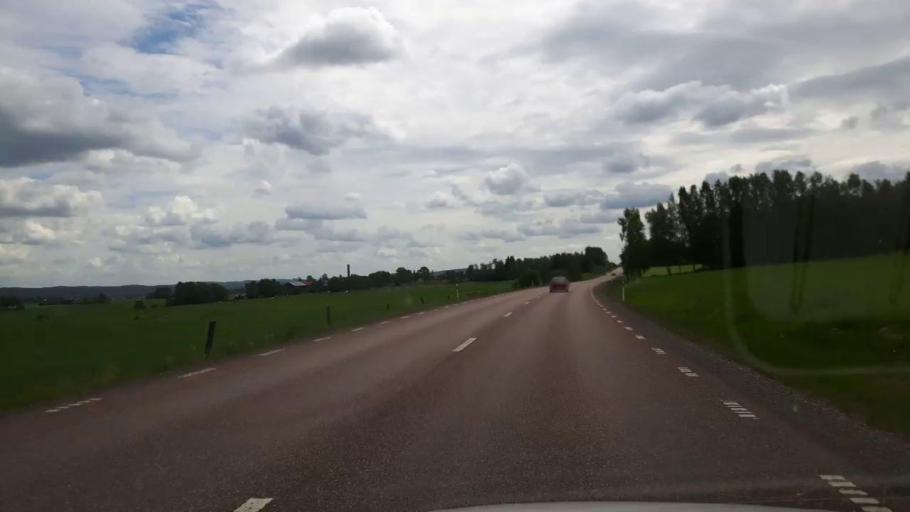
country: SE
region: Dalarna
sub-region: Hedemora Kommun
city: Hedemora
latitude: 60.3094
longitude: 15.9711
